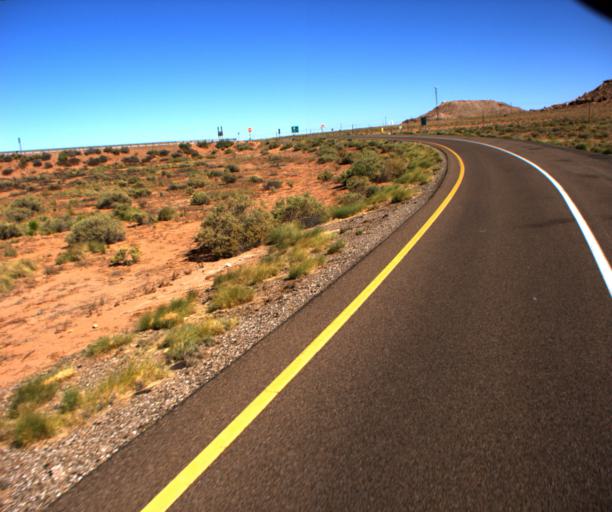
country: US
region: Arizona
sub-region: Coconino County
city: LeChee
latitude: 35.0681
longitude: -110.8332
